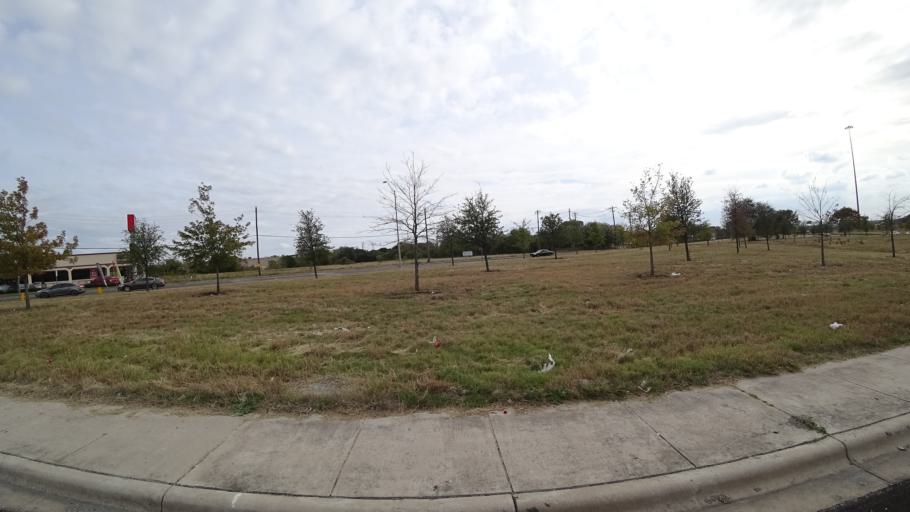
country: US
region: Texas
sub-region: Travis County
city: Wells Branch
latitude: 30.4410
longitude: -97.6668
